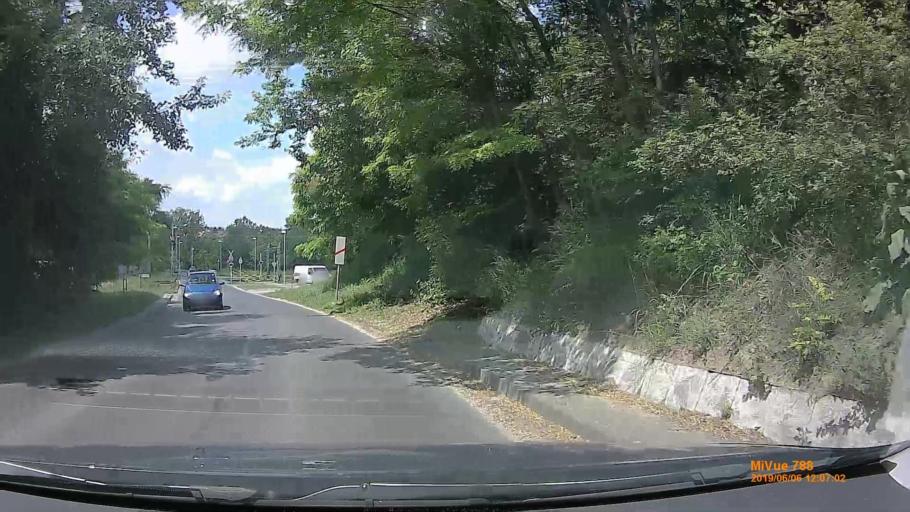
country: HU
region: Pest
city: Kerepes
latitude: 47.5647
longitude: 19.2746
